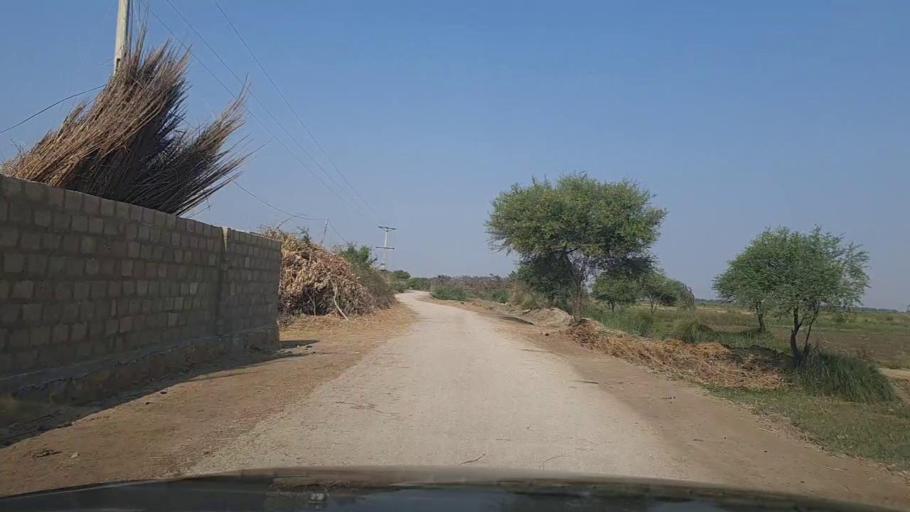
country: PK
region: Sindh
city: Thatta
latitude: 24.6159
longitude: 67.8190
